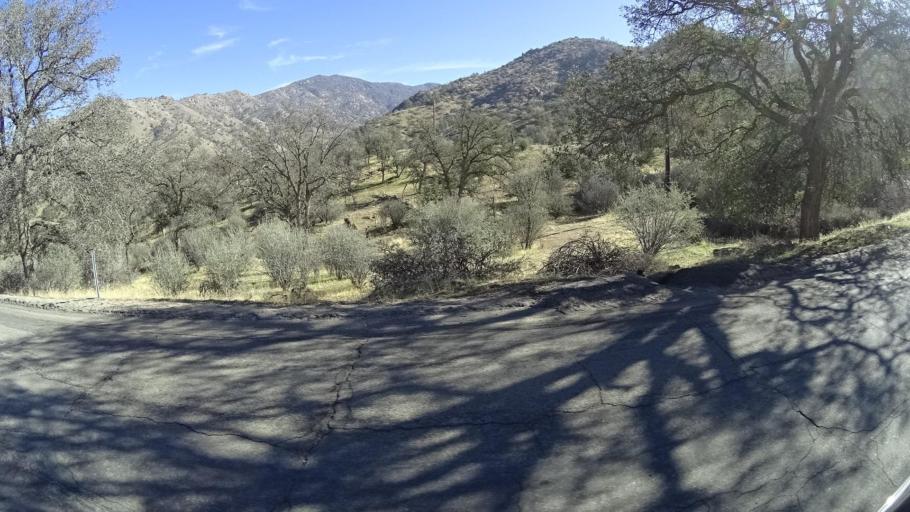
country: US
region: California
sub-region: Kern County
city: Bodfish
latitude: 35.5318
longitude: -118.6296
